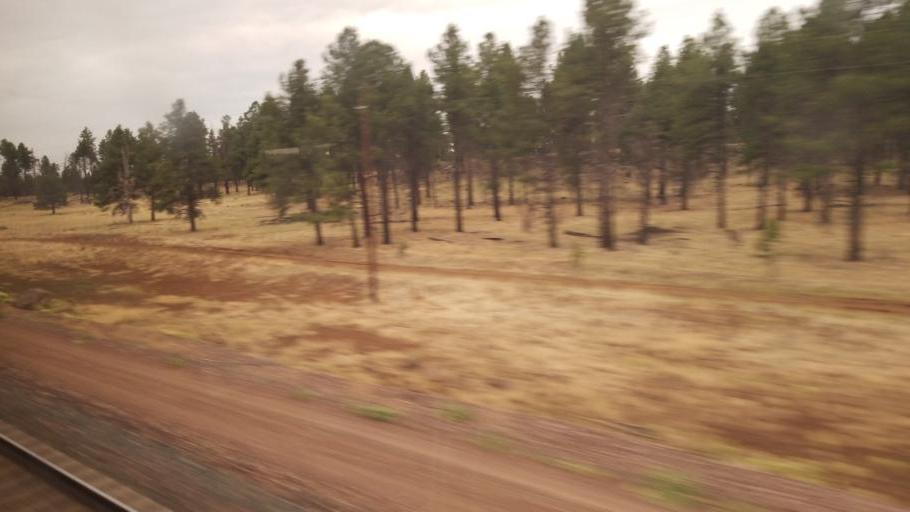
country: US
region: Arizona
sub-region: Coconino County
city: Parks
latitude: 35.2430
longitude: -112.0331
